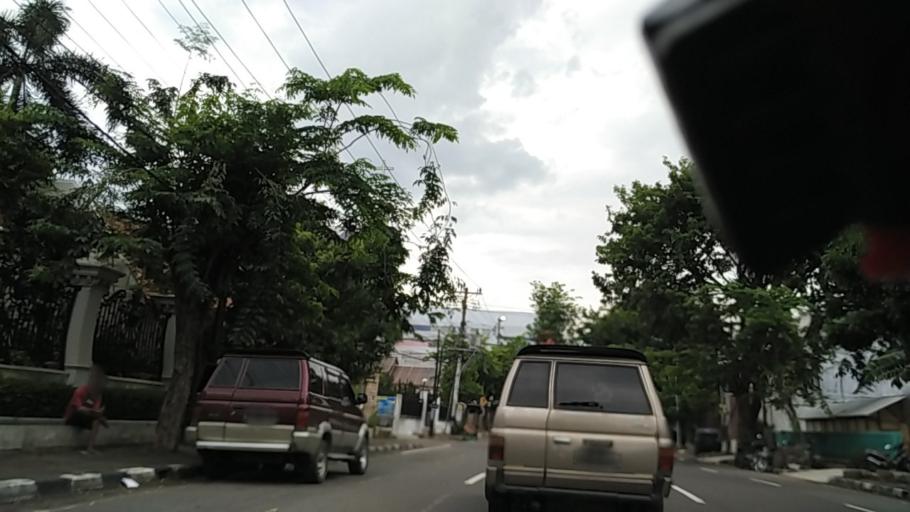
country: ID
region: Central Java
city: Semarang
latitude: -6.9994
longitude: 110.4335
